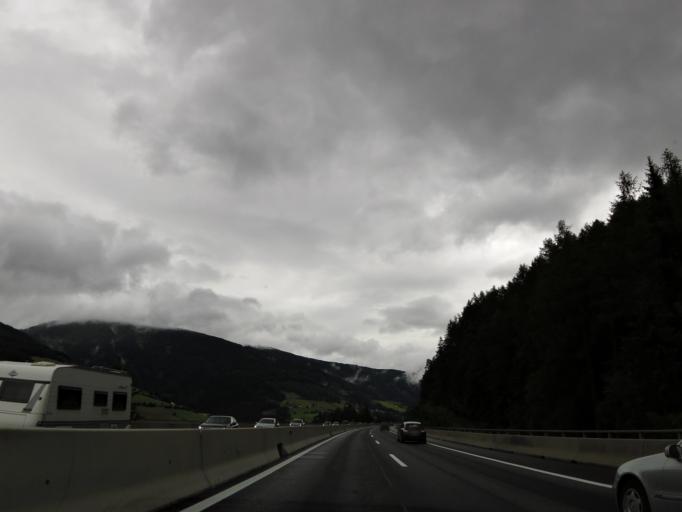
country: AT
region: Tyrol
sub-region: Politischer Bezirk Innsbruck Land
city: Schoenberg im Stubaital
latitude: 47.1728
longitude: 11.4237
